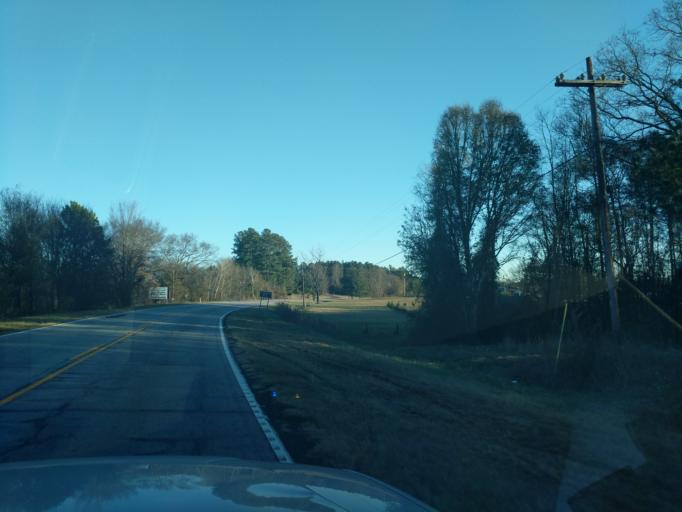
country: US
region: Georgia
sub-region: Hart County
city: Reed Creek
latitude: 34.5586
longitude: -82.8713
